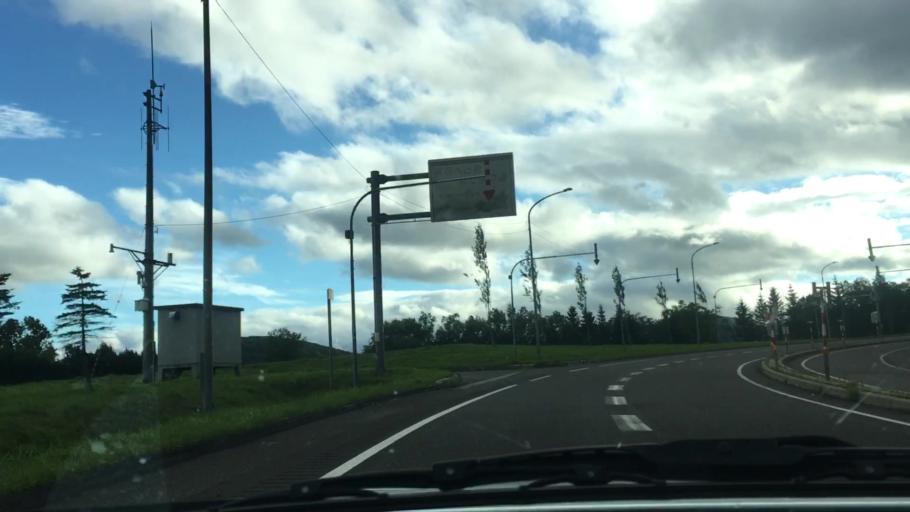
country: JP
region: Hokkaido
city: Otofuke
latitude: 43.1614
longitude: 142.8037
